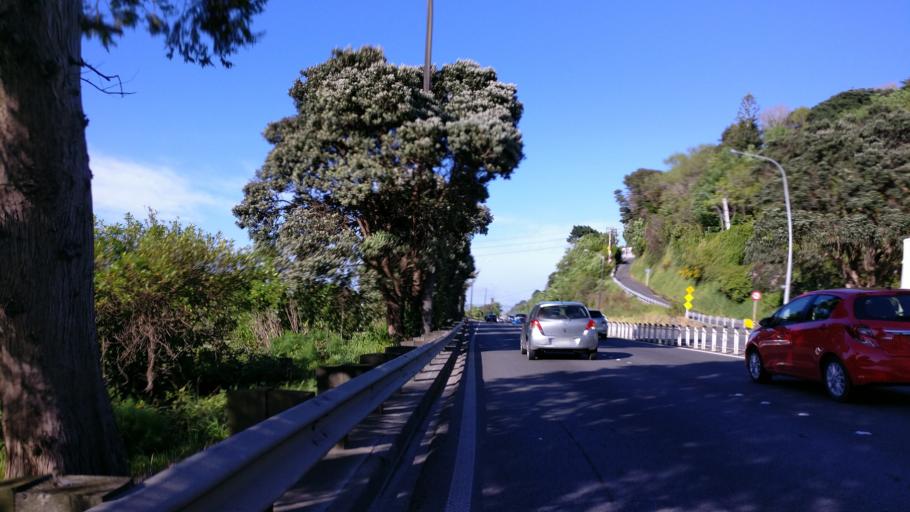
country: NZ
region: Wellington
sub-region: Lower Hutt City
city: Lower Hutt
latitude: -41.1977
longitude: 174.9161
